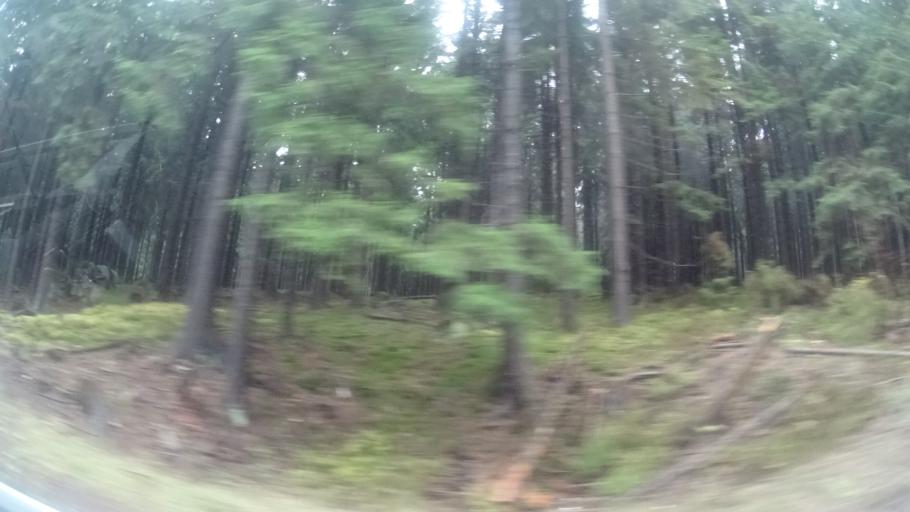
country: DE
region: Thuringia
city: Steinheid
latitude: 50.4864
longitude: 11.1034
